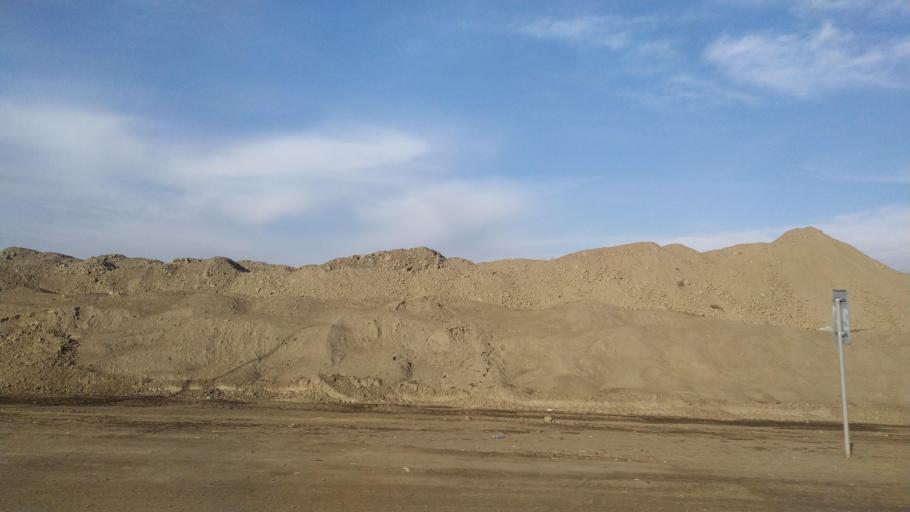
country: KZ
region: Almaty Oblysy
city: Burunday
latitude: 43.2240
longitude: 76.7285
